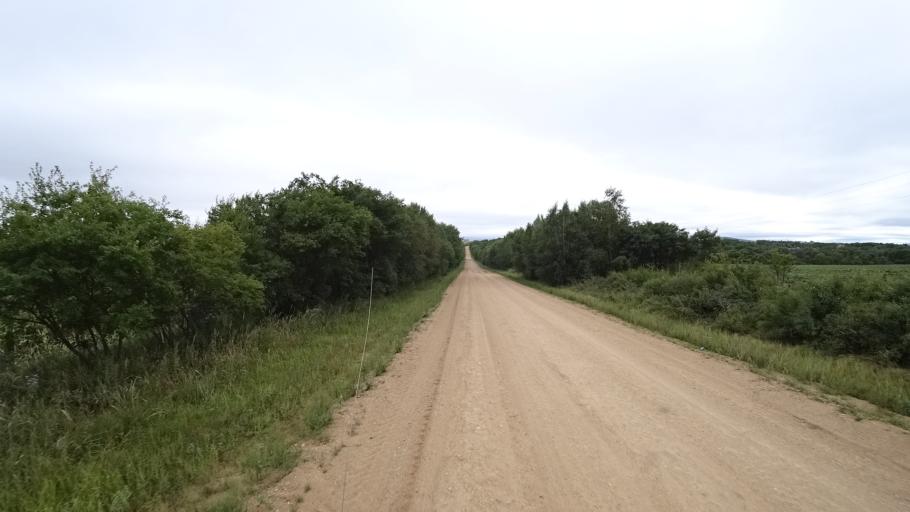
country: RU
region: Primorskiy
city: Monastyrishche
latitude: 44.0890
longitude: 132.5978
